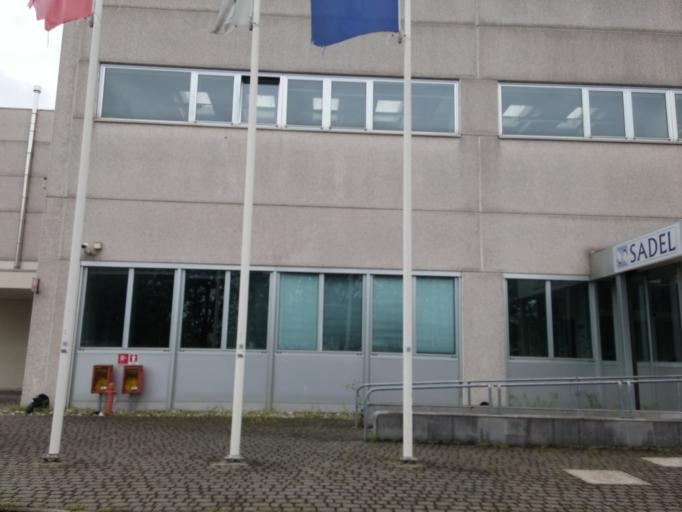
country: IT
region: Emilia-Romagna
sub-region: Provincia di Bologna
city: Progresso
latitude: 44.5593
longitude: 11.3757
